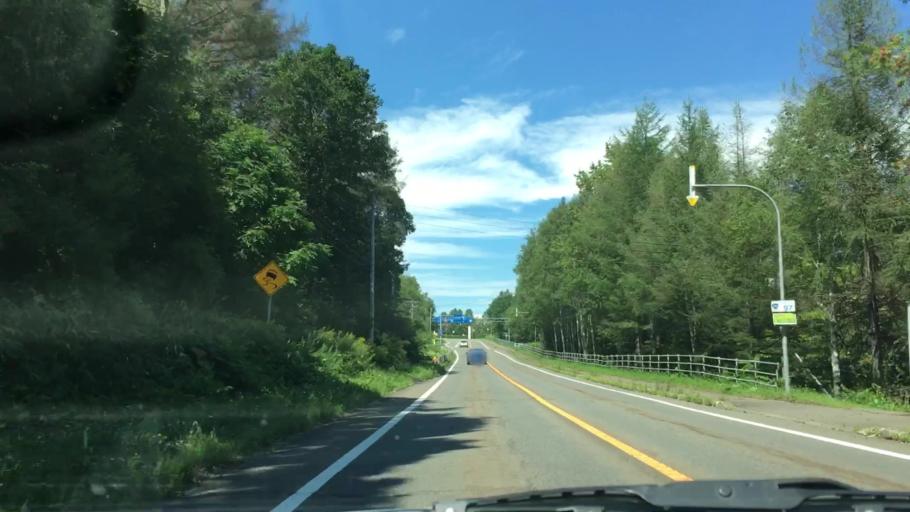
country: JP
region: Hokkaido
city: Otofuke
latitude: 43.2348
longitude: 143.5393
